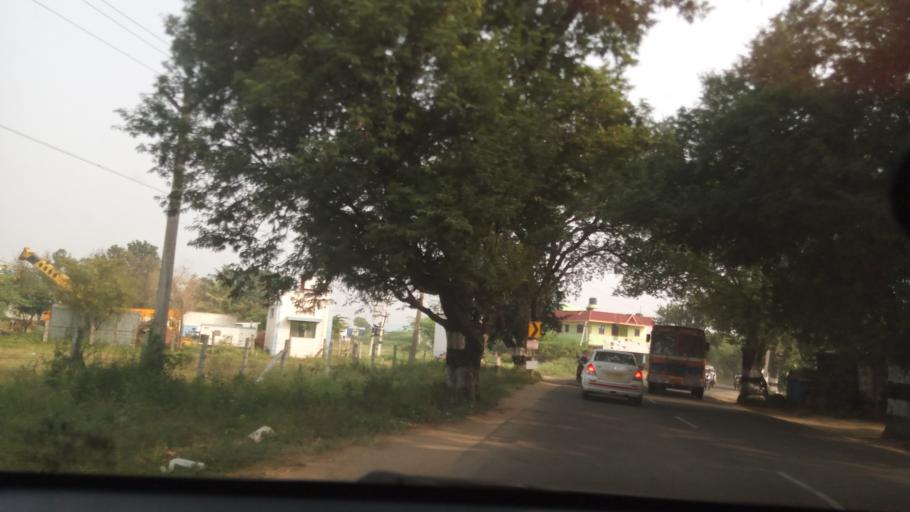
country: IN
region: Tamil Nadu
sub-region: Coimbatore
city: Periyanayakkanpalaiyam
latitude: 11.1444
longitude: 77.0414
